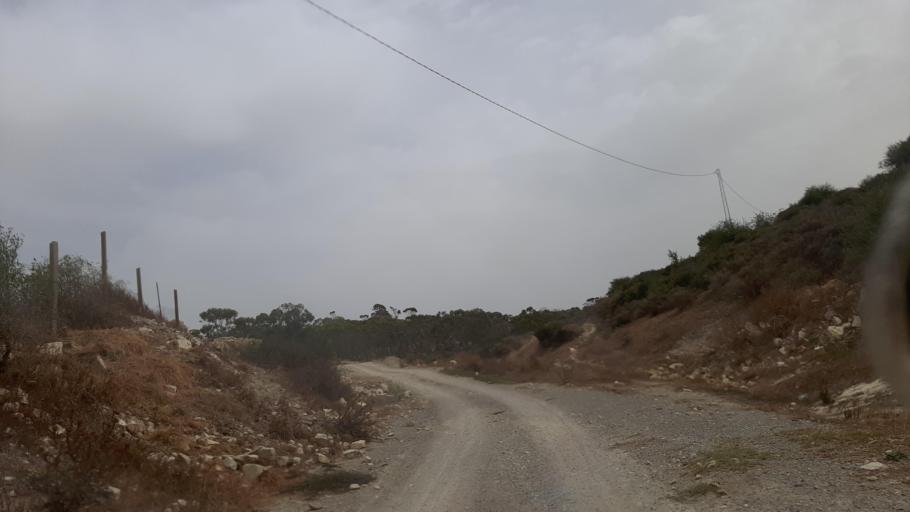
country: TN
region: Tunis
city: La Mohammedia
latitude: 36.5683
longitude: 10.1395
